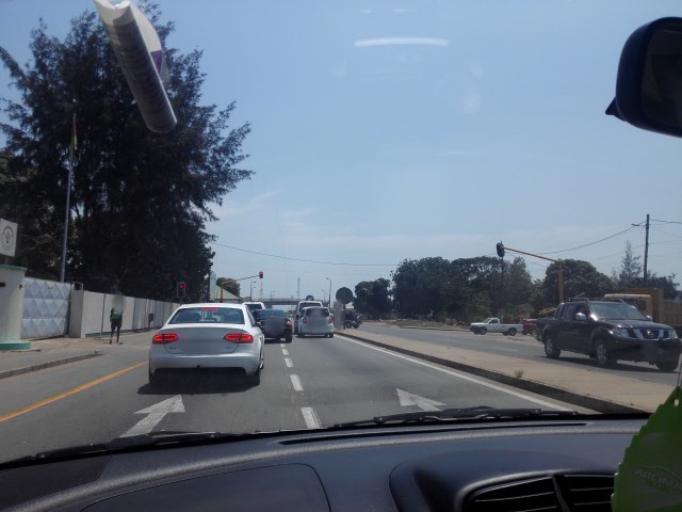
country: MZ
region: Maputo City
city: Maputo
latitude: -25.9416
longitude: 32.5437
